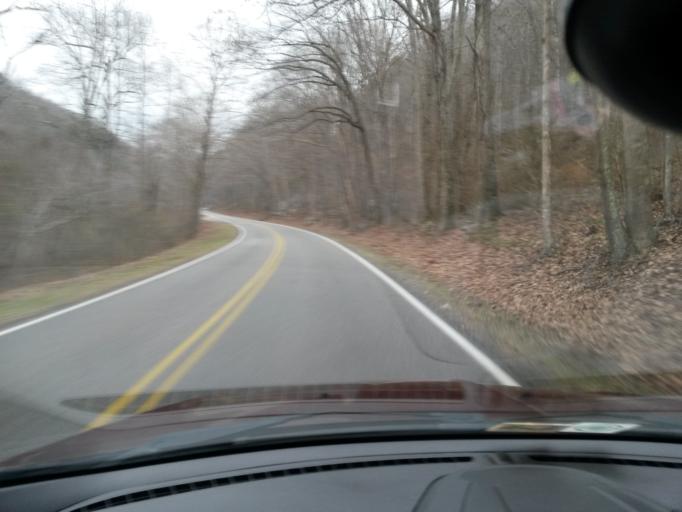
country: US
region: Virginia
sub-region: Rockbridge County
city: East Lexington
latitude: 37.9664
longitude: -79.4951
